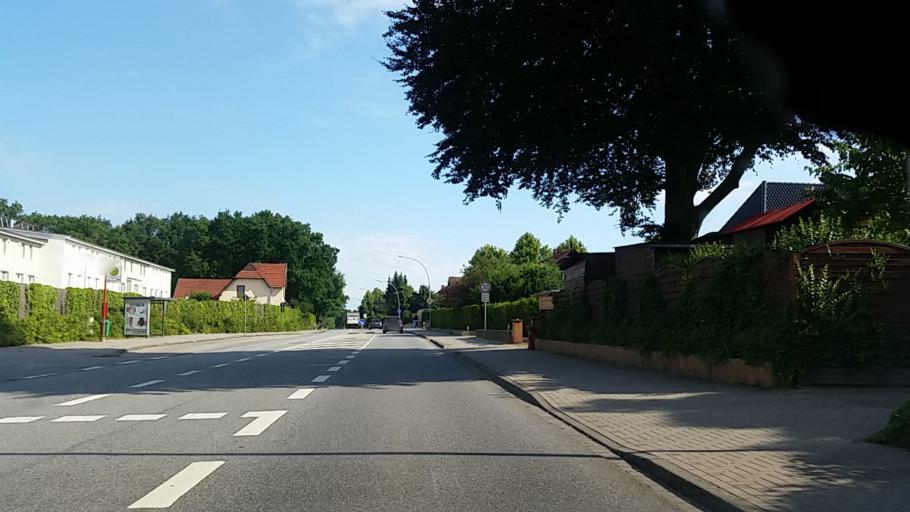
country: DE
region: Hamburg
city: Langenhorn
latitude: 53.6961
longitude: 10.0282
